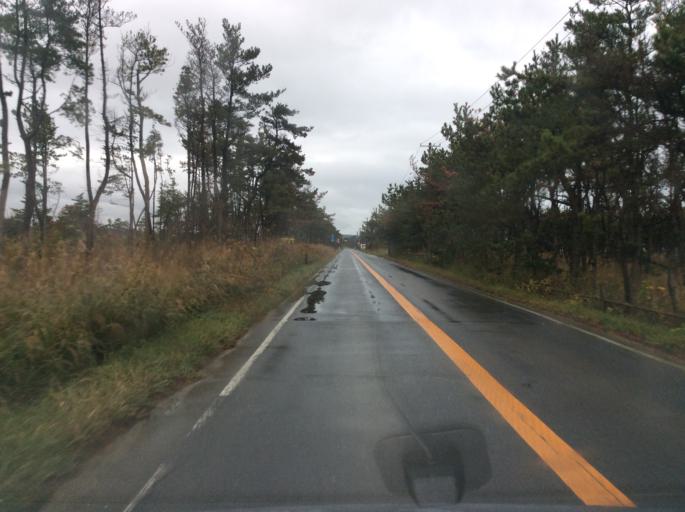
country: JP
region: Fukushima
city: Iwaki
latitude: 37.0772
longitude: 140.9784
